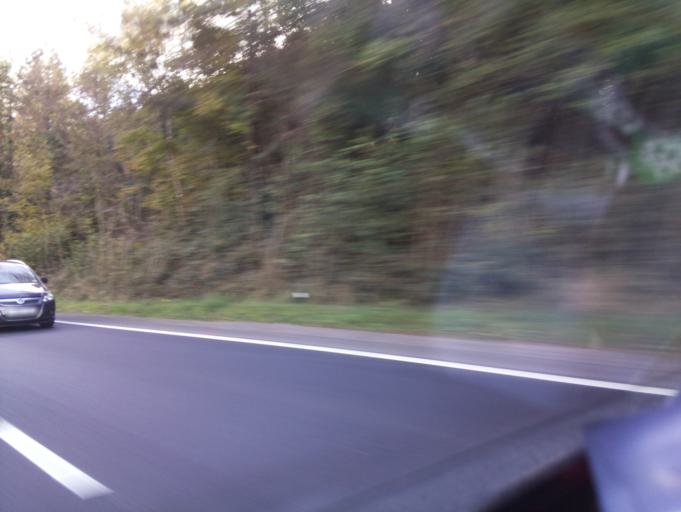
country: GB
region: Wales
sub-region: Merthyr Tydfil County Borough
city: Treharris
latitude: 51.6717
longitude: -3.3342
